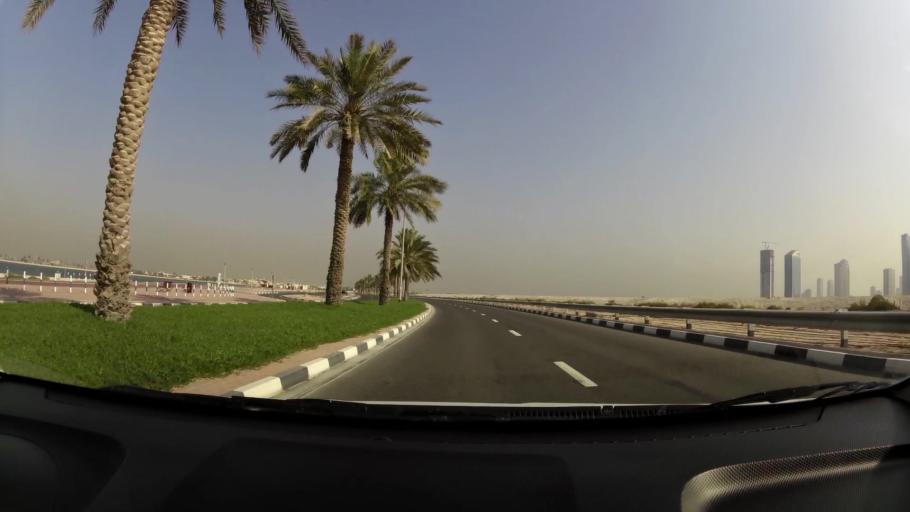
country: AE
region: Ash Shariqah
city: Sharjah
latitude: 25.3034
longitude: 55.3585
